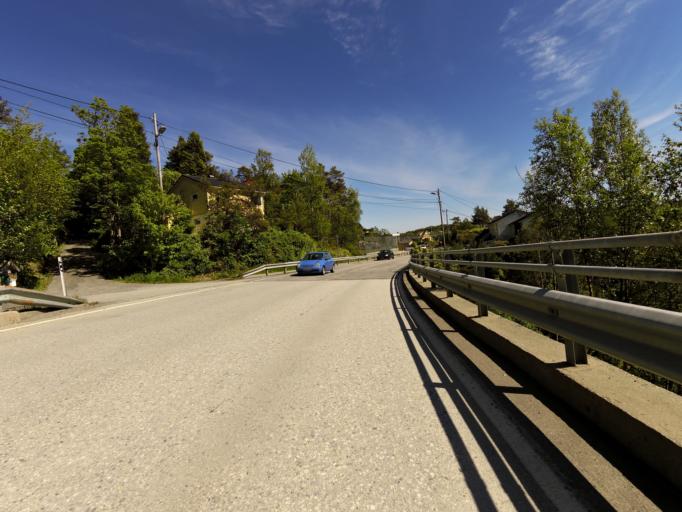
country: NO
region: Hordaland
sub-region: Stord
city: Sagvag
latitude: 59.7806
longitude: 5.3901
